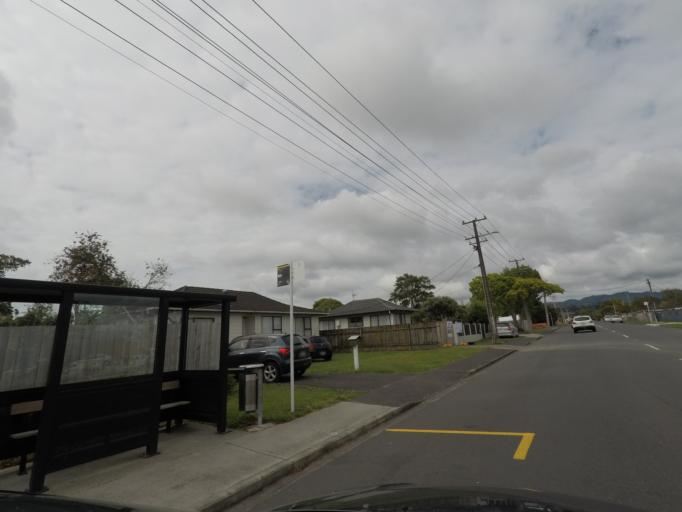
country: NZ
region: Auckland
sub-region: Auckland
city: Waitakere
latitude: -36.8982
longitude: 174.6248
